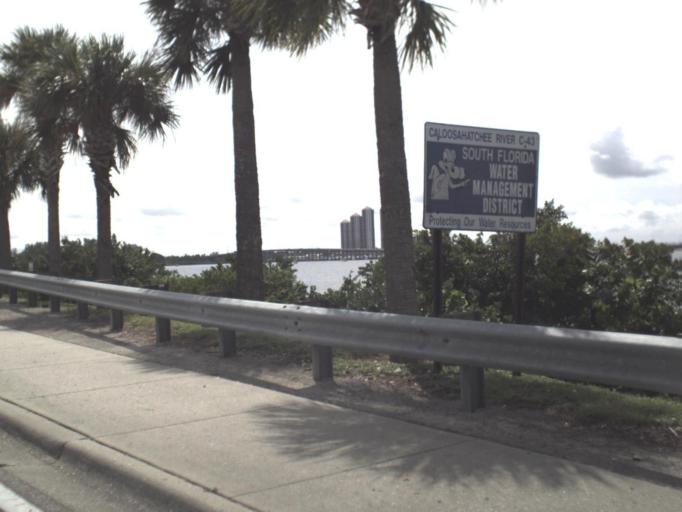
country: US
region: Florida
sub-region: Lee County
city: North Fort Myers
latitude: 26.6596
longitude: -81.8751
